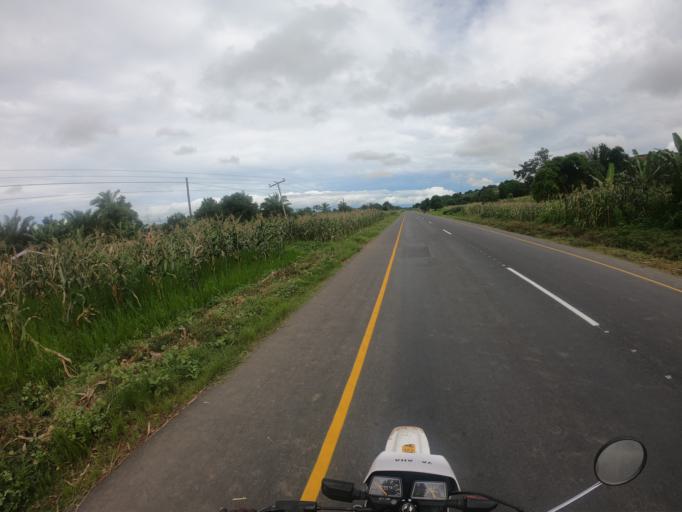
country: TZ
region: Mbeya
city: Kyela
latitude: -9.6688
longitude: 33.8207
